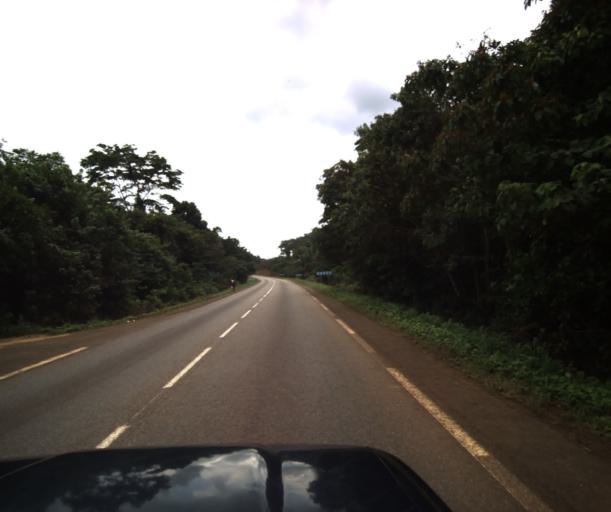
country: CM
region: Littoral
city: Edea
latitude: 3.8371
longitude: 10.4186
